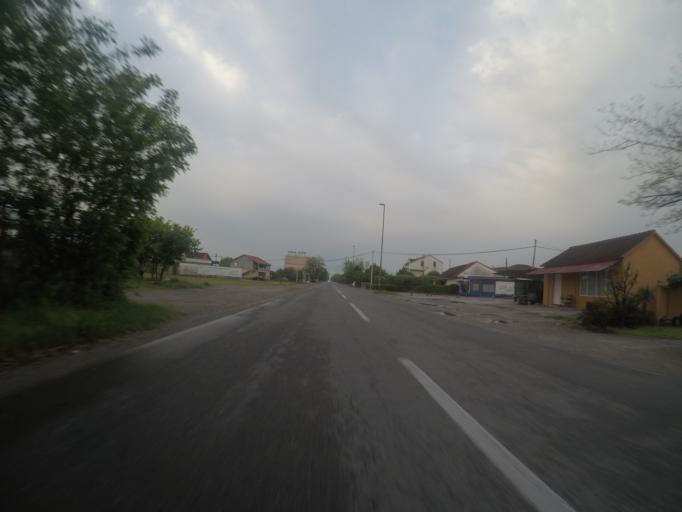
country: ME
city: Mojanovici
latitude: 42.3424
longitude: 19.2217
